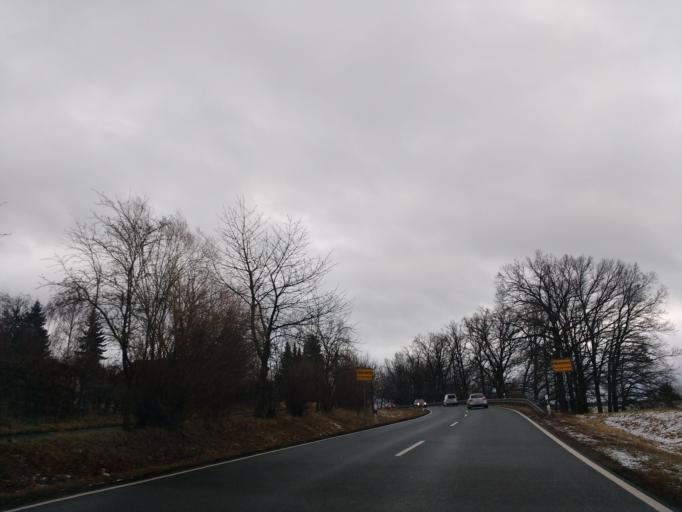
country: DE
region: Bavaria
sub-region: Regierungsbezirk Mittelfranken
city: Herzogenaurach
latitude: 49.5898
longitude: 10.8553
